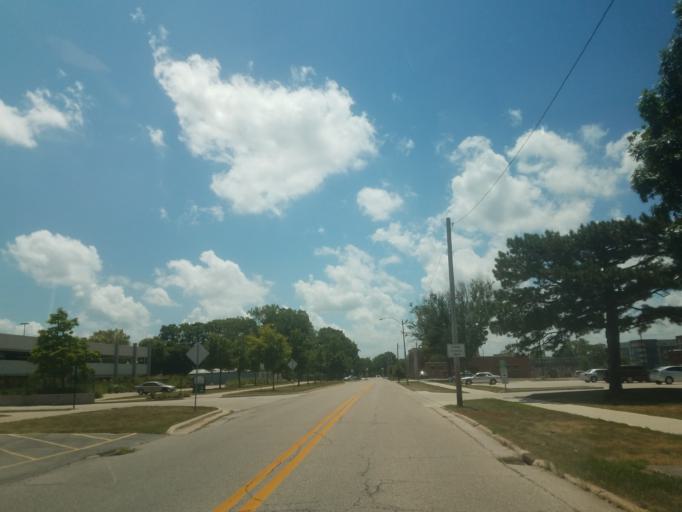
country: US
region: Illinois
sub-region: McLean County
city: Normal
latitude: 40.5067
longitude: -88.9931
